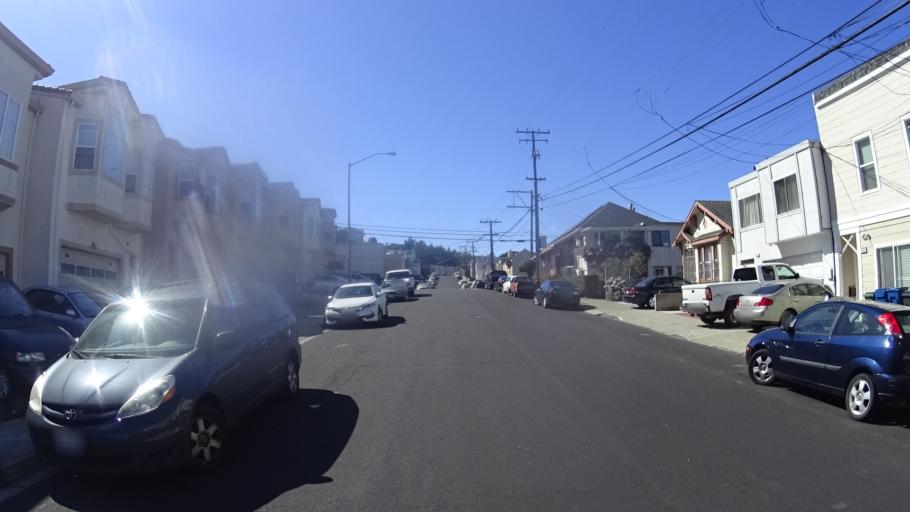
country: US
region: California
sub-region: San Mateo County
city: Daly City
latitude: 37.7037
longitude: -122.4539
